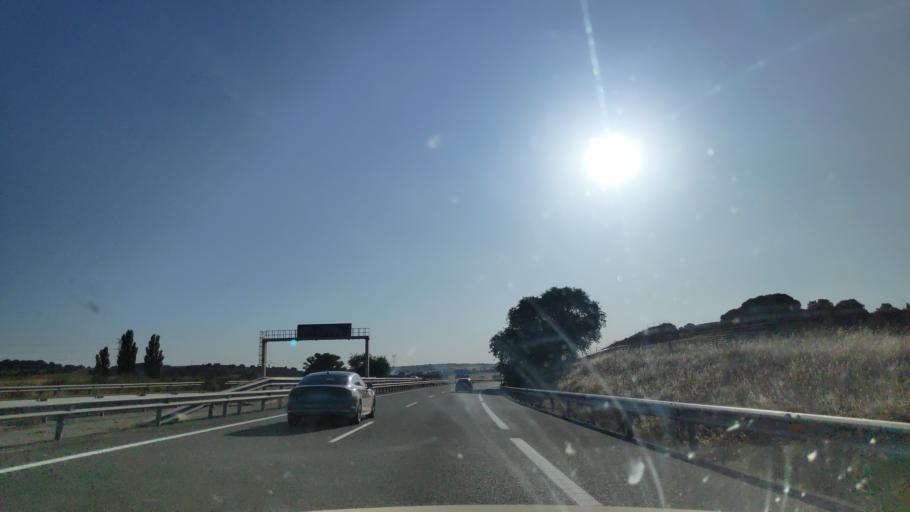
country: ES
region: Castille-La Mancha
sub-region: Provincia de Cuenca
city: Zafra de Zancara
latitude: 39.8594
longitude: -2.5497
